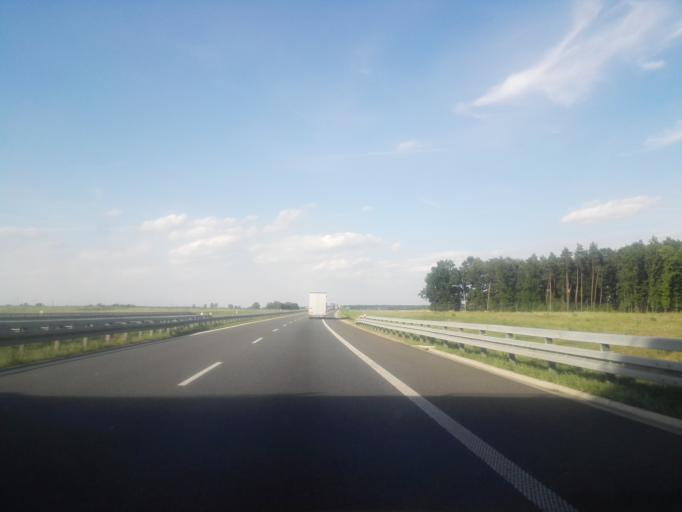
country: PL
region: Lower Silesian Voivodeship
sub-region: Powiat olesnicki
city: Twardogora
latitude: 51.2740
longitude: 17.5580
